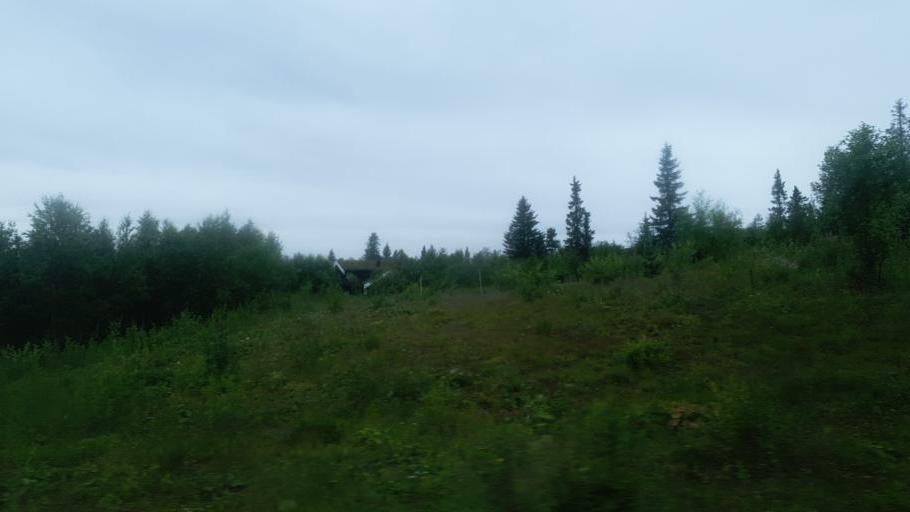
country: NO
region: Oppland
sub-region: Vestre Slidre
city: Slidre
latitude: 61.2390
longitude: 8.9160
